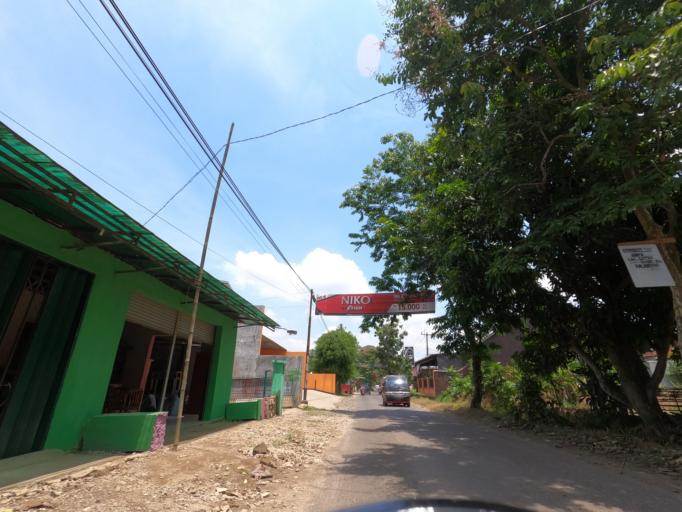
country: ID
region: West Java
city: Pamanukan
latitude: -6.5400
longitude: 107.7688
